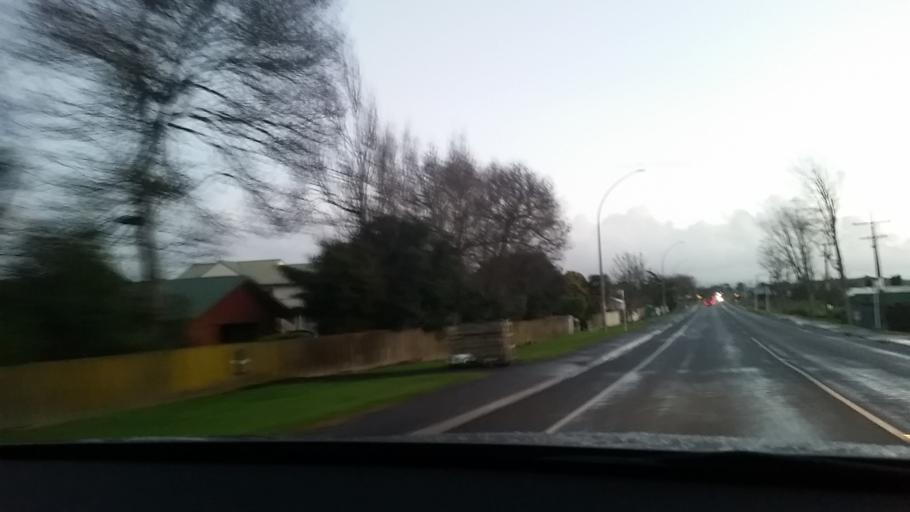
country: NZ
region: Waikato
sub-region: Hamilton City
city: Hamilton
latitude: -37.8049
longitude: 175.2422
